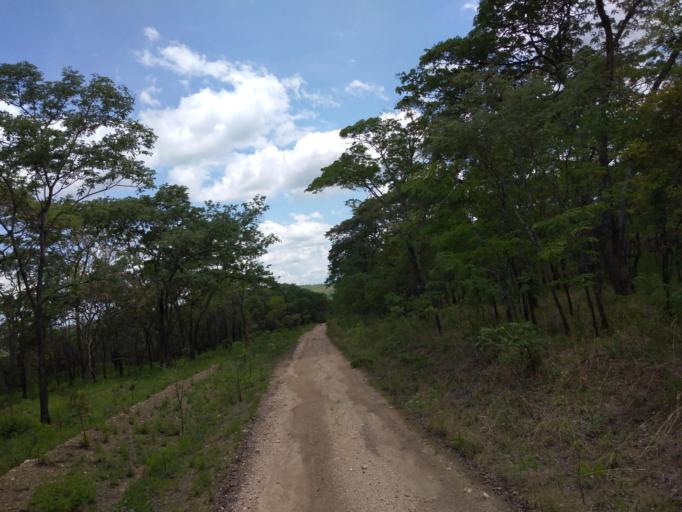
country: ZM
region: Central
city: Mkushi
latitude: -14.0844
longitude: 29.9769
